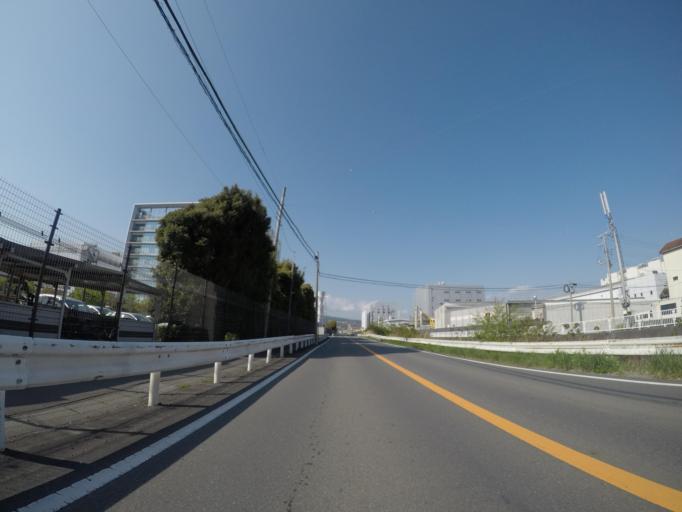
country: JP
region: Shizuoka
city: Numazu
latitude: 35.1105
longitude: 138.8486
